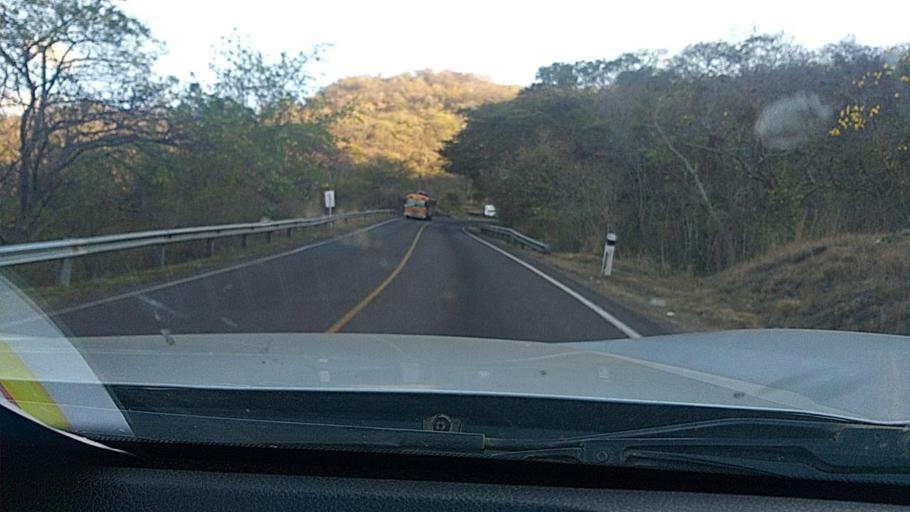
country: NI
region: Esteli
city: Condega
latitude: 13.2591
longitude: -86.3548
